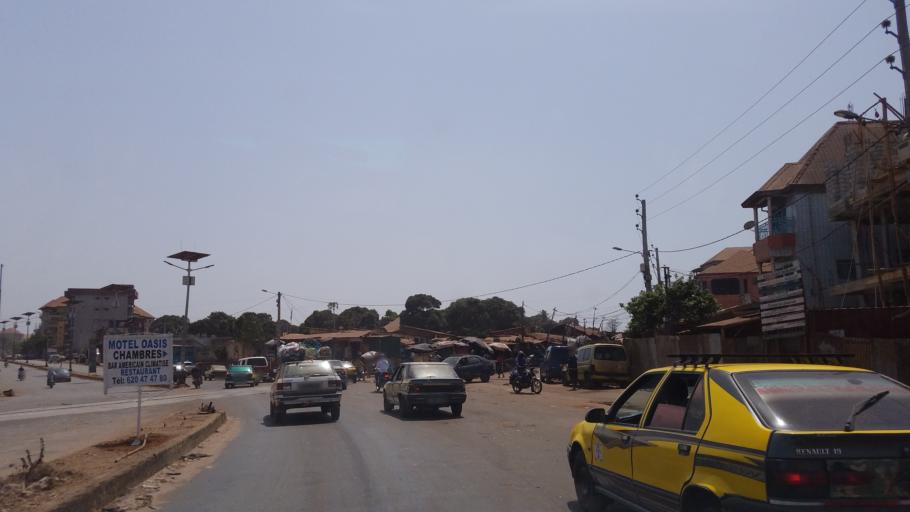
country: GN
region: Conakry
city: Conakry
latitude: 9.6486
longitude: -13.5849
